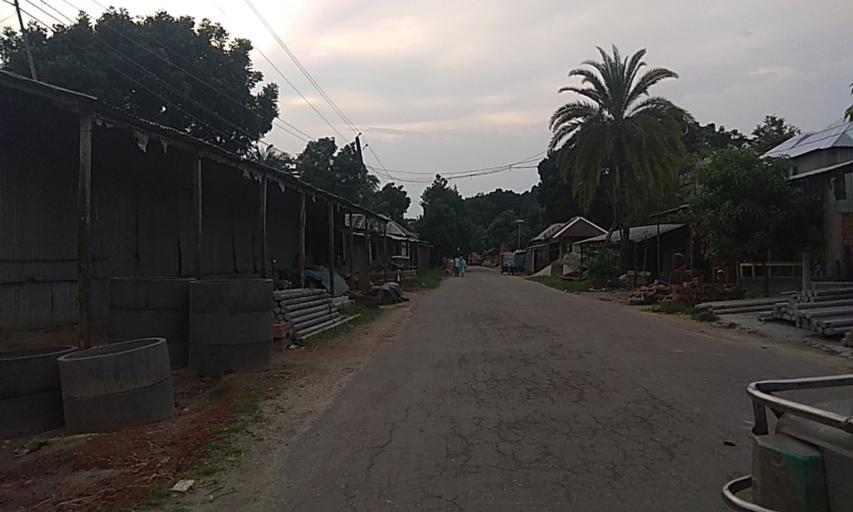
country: BD
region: Dhaka
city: Dohar
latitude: 23.4617
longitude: 89.9961
